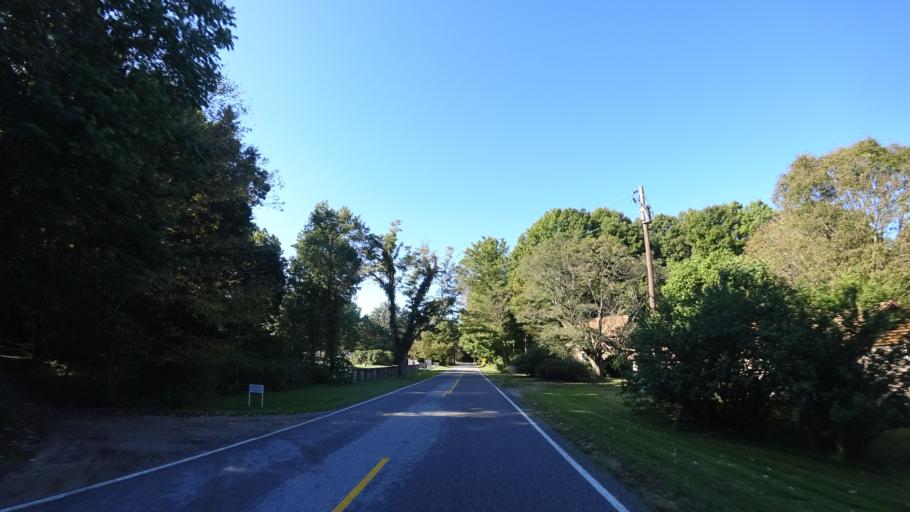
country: US
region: Michigan
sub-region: Berrien County
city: Benton Heights
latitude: 42.1557
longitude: -86.4180
